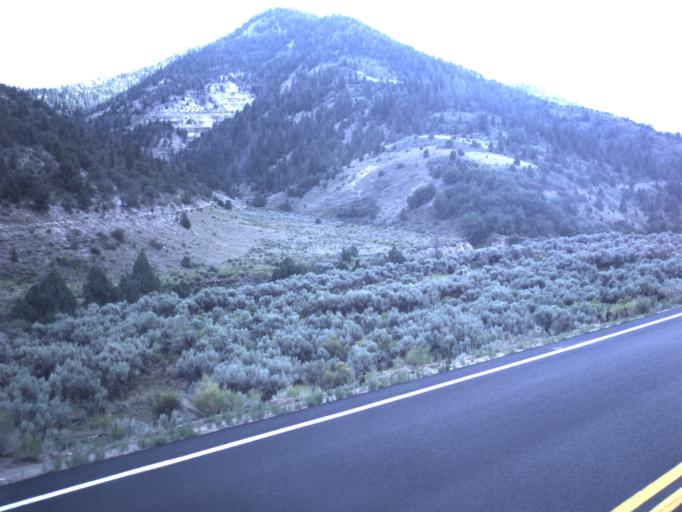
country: US
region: Utah
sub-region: Duchesne County
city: Duchesne
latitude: 39.9536
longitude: -110.6518
